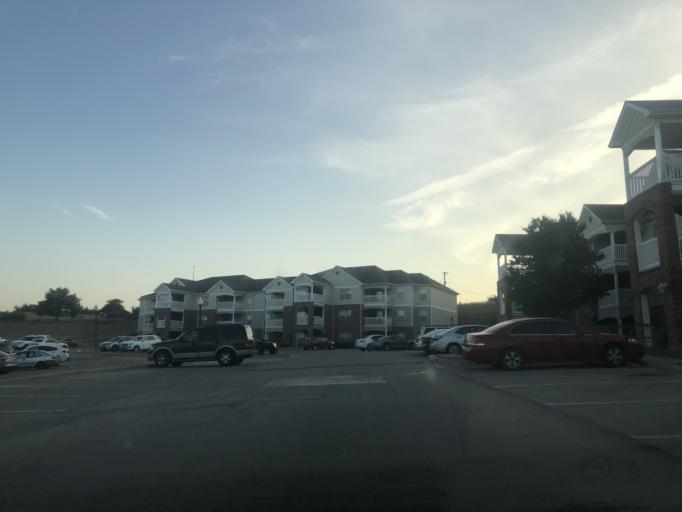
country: US
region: Texas
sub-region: Tarrant County
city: Sansom Park
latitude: 32.8041
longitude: -97.4179
